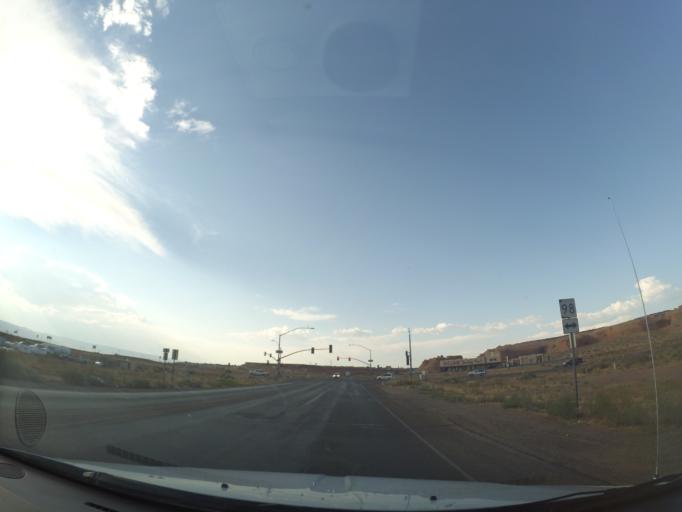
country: US
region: Arizona
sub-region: Coconino County
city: Page
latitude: 36.8944
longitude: -111.4447
